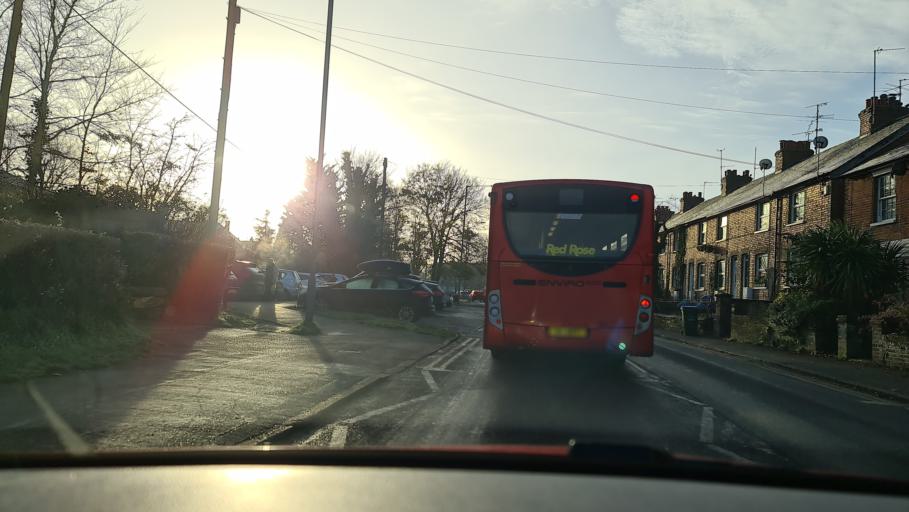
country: GB
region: England
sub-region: Buckinghamshire
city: Wendover
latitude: 51.7659
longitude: -0.7441
